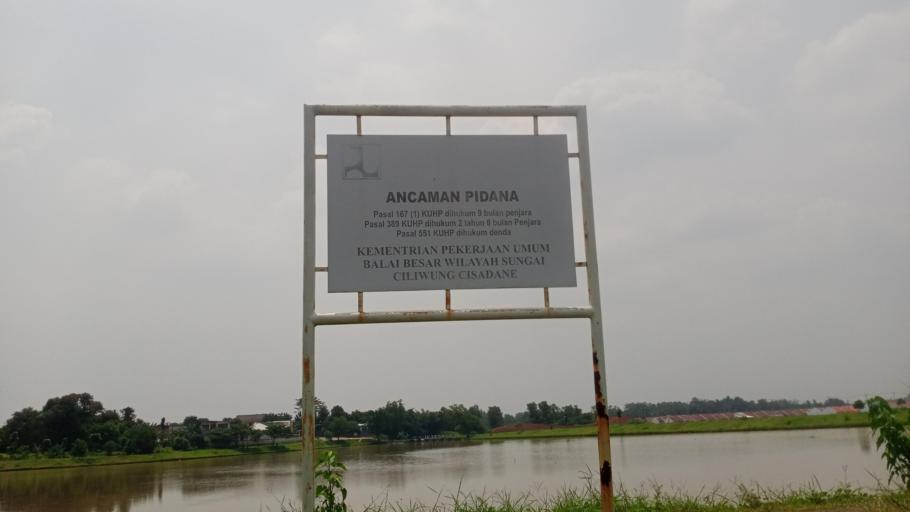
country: ID
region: West Java
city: Cileungsir
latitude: -6.3523
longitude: 107.0372
